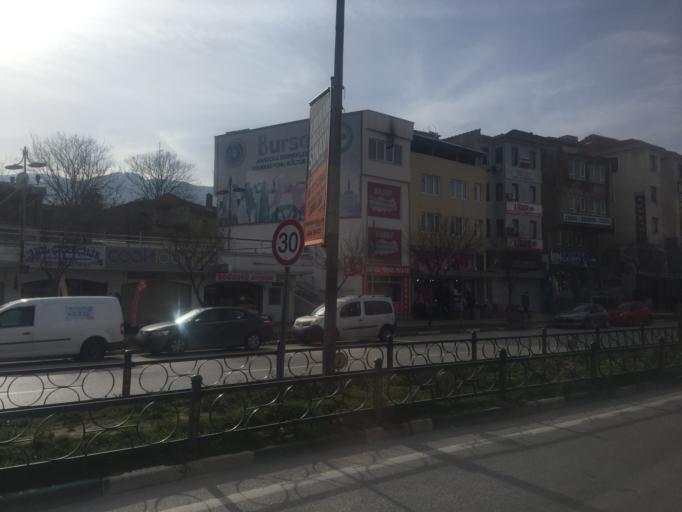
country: TR
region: Bursa
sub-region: Osmangazi
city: Bursa
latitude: 40.1876
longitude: 29.0676
